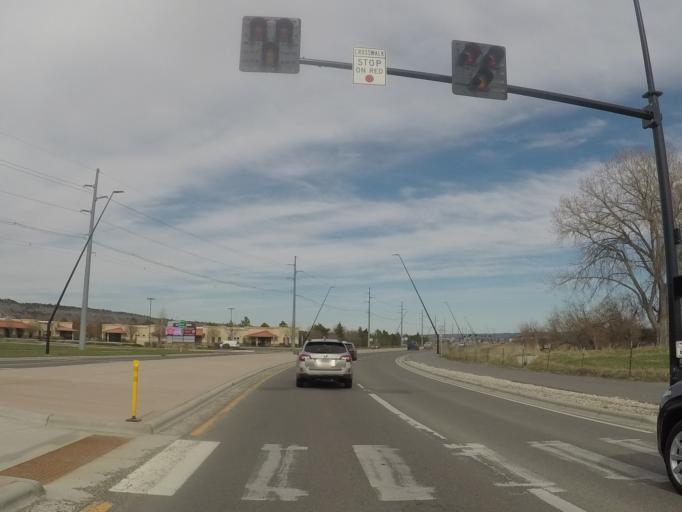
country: US
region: Montana
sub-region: Yellowstone County
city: Billings
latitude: 45.7839
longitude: -108.6107
